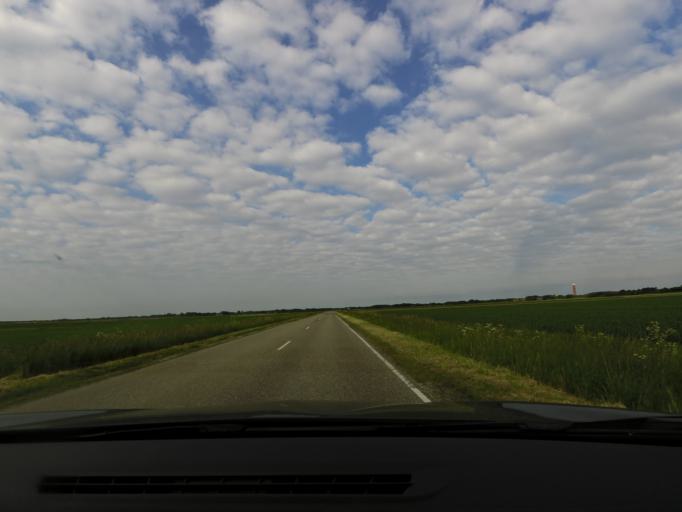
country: NL
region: South Holland
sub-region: Gemeente Goeree-Overflakkee
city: Ouddorp
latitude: 51.8126
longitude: 3.8848
